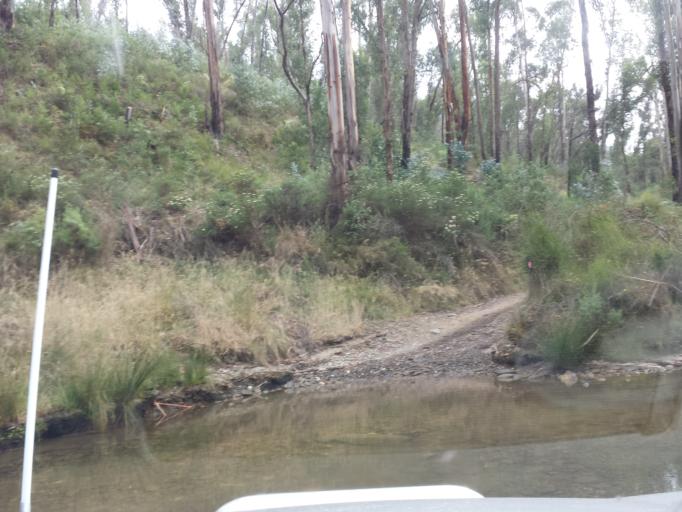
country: AU
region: Victoria
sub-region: Wellington
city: Heyfield
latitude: -37.7574
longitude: 146.4027
